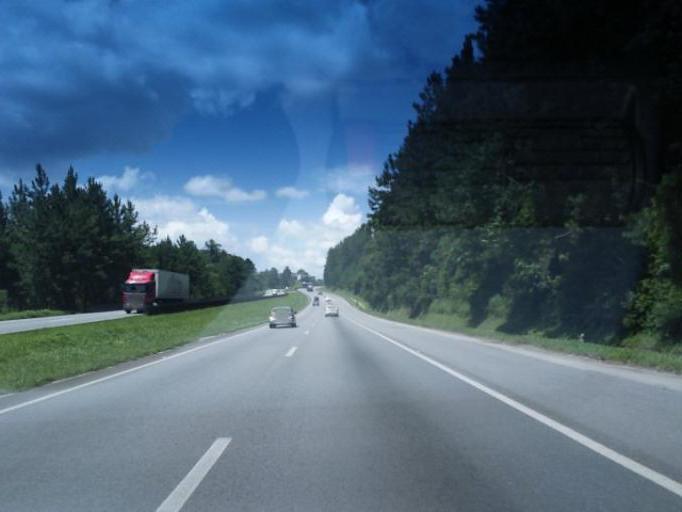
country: BR
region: Sao Paulo
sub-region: Juquitiba
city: Juquitiba
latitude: -23.9464
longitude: -47.0987
